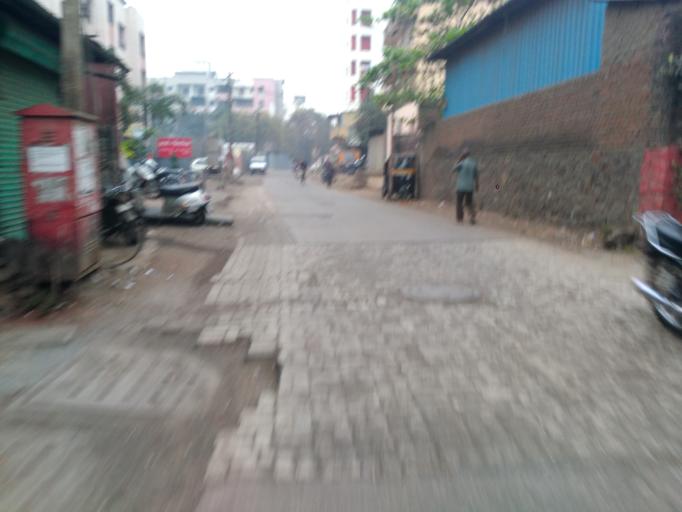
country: IN
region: Maharashtra
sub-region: Pune Division
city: Pune
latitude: 18.4579
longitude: 73.8881
